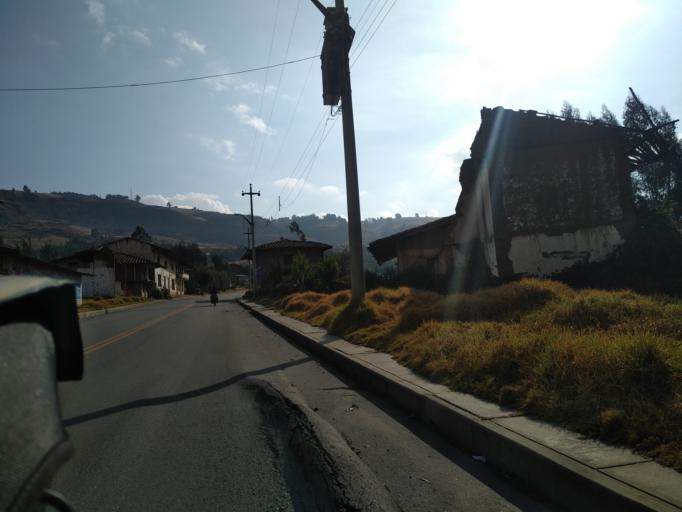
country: PE
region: La Libertad
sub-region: Provincia de Otuzco
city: Agallpampa
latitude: -7.9948
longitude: -78.5221
